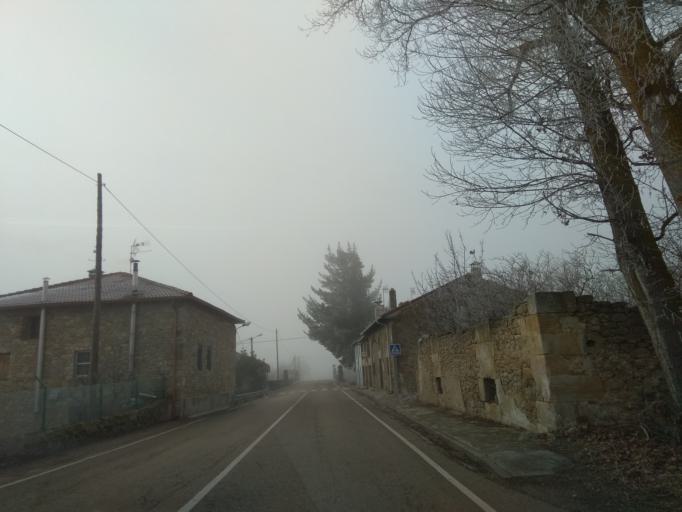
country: ES
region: Castille and Leon
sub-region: Provincia de Burgos
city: Espinosa de los Monteros
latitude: 43.0417
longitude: -3.4920
